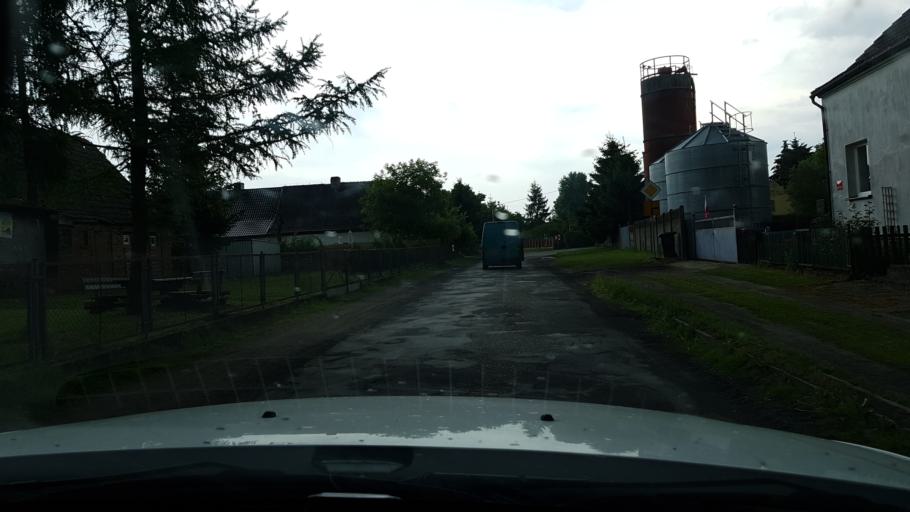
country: PL
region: West Pomeranian Voivodeship
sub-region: Powiat stargardzki
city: Marianowo
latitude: 53.3186
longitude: 15.1799
